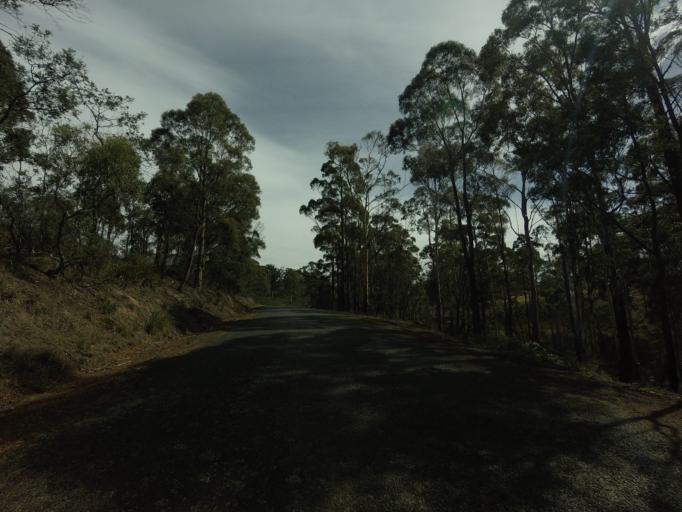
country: AU
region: Tasmania
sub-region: Sorell
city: Sorell
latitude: -42.5599
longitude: 147.6803
